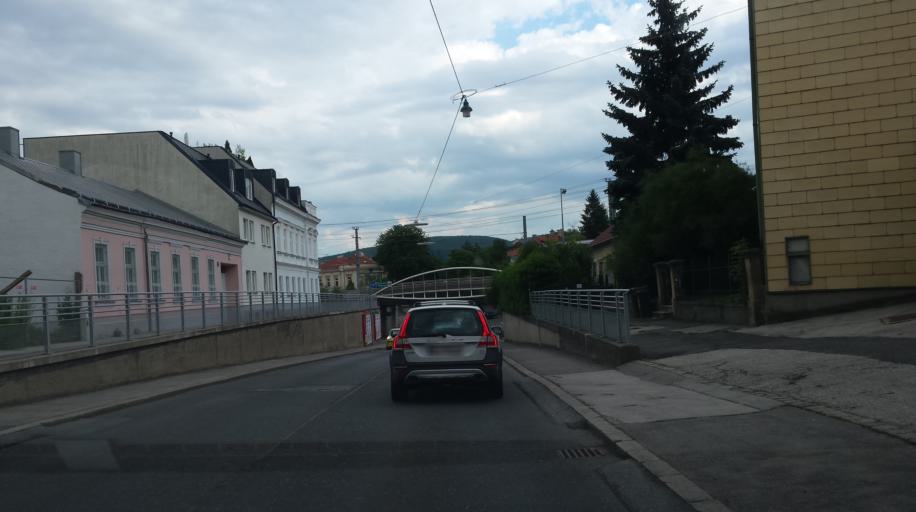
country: AT
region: Lower Austria
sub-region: Politischer Bezirk Wien-Umgebung
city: Purkersdorf
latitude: 48.2112
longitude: 16.2237
